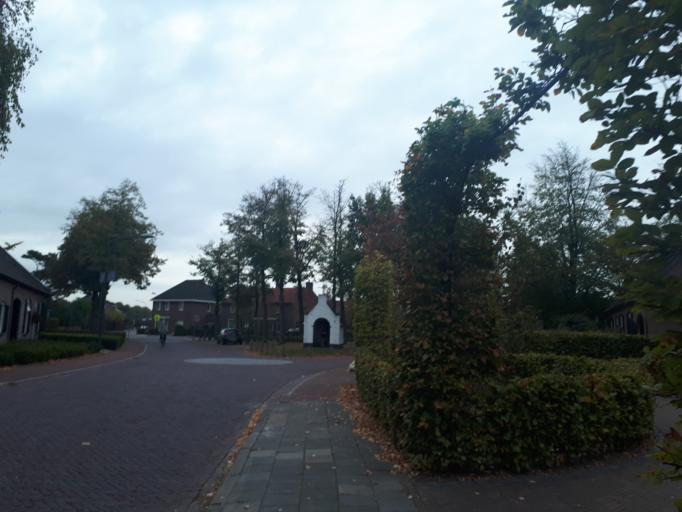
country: NL
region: North Brabant
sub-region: Gemeente Eersel
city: Eersel
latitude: 51.3570
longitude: 5.3150
